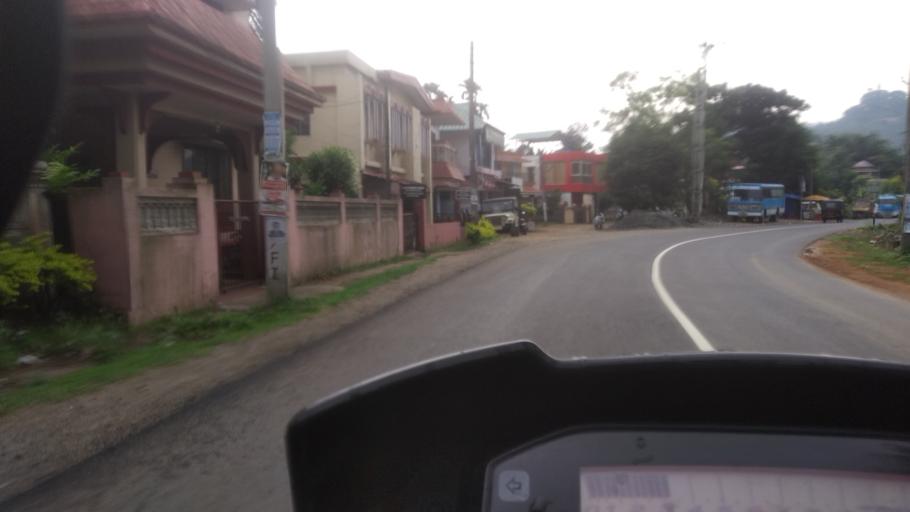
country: IN
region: Tamil Nadu
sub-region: Theni
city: Gudalur
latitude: 9.5841
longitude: 77.1061
